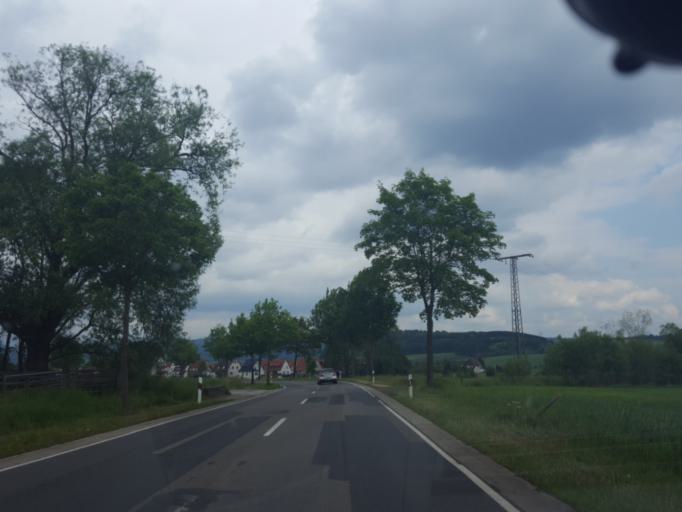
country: DE
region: Lower Saxony
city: Eisdorf am Harz
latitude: 51.7531
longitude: 10.1704
